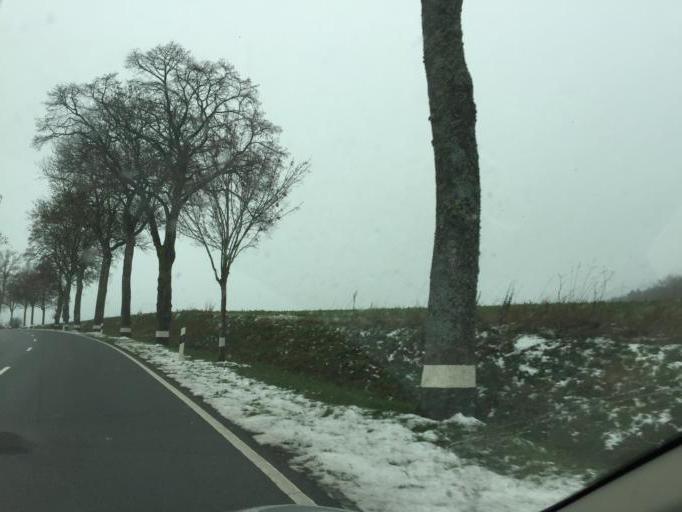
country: LU
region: Diekirch
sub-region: Canton de Redange
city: Grosbous
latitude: 49.8302
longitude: 5.9794
